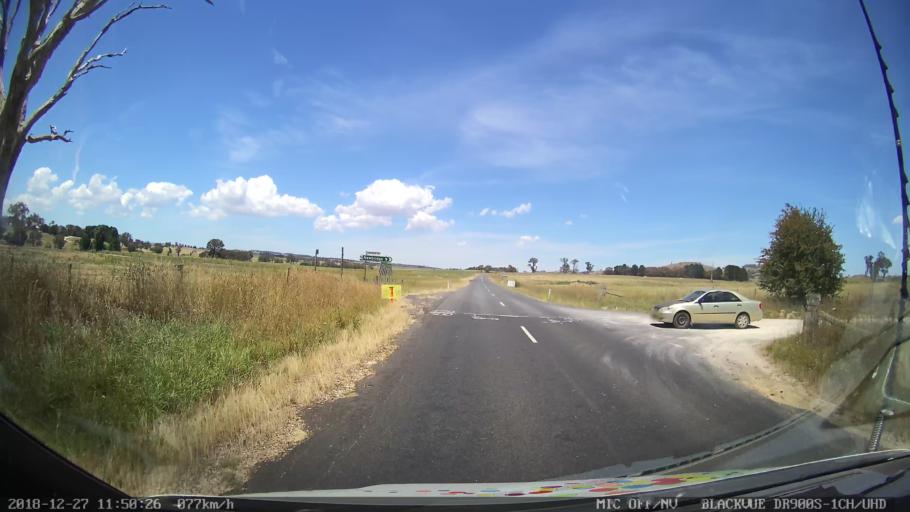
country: AU
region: New South Wales
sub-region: Bathurst Regional
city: Perthville
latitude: -33.6322
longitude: 149.4306
